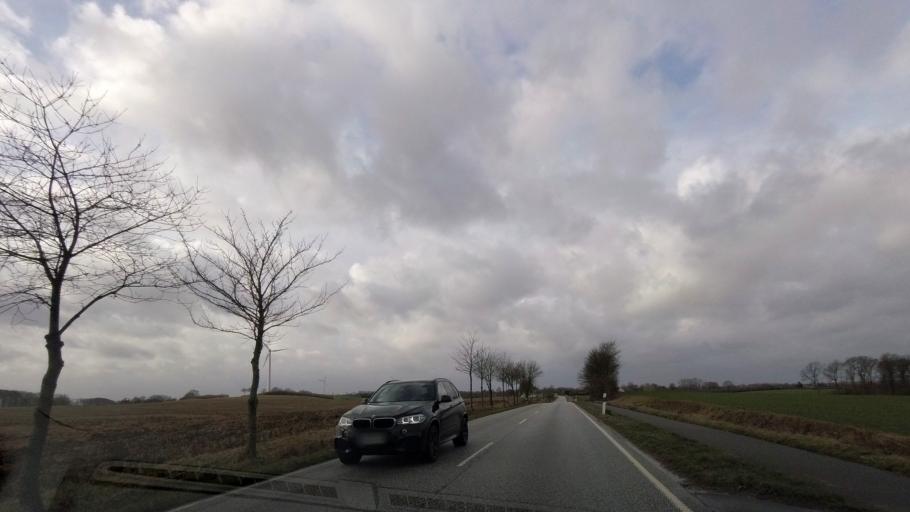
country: DE
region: Schleswig-Holstein
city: Dollrottfeld
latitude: 54.6435
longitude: 9.8282
